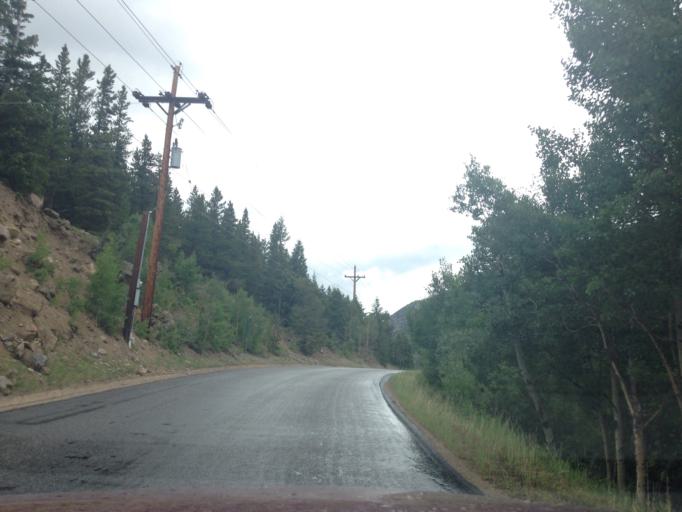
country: US
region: Colorado
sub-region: Clear Creek County
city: Georgetown
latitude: 39.6950
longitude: -105.6965
